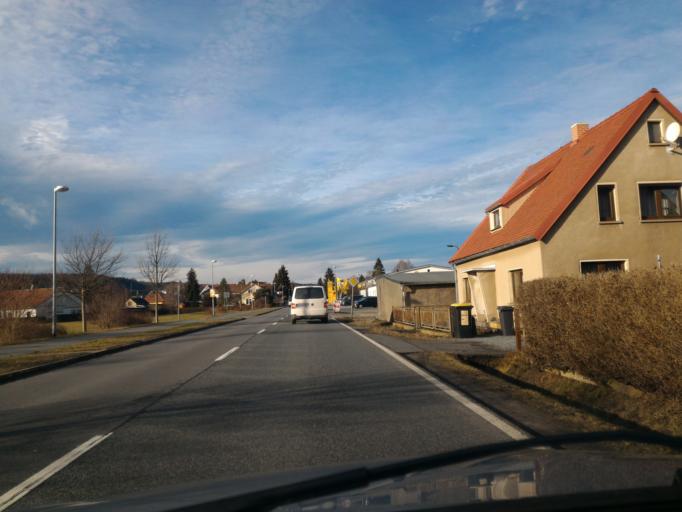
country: DE
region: Saxony
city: Sohland
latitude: 51.0546
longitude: 14.4067
